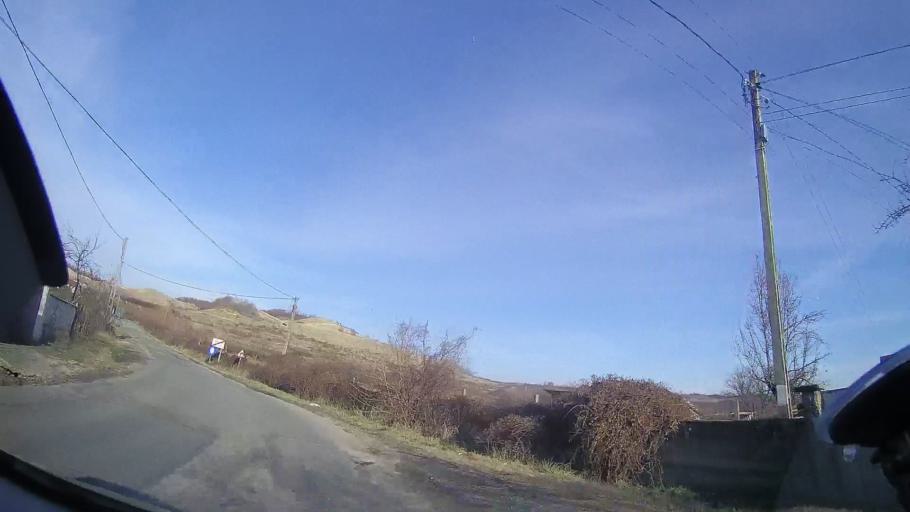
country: RO
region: Bihor
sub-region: Comuna Tileagd
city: Tileagd
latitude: 47.0812
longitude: 22.2224
